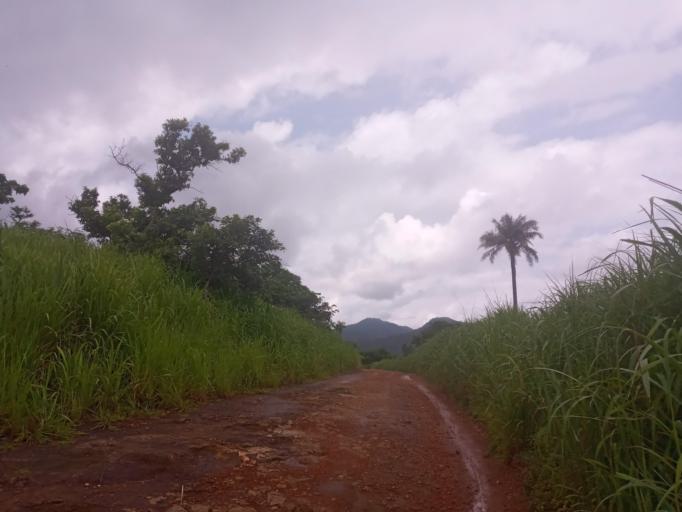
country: SL
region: Northern Province
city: Bumbuna
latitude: 8.9355
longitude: -11.7500
